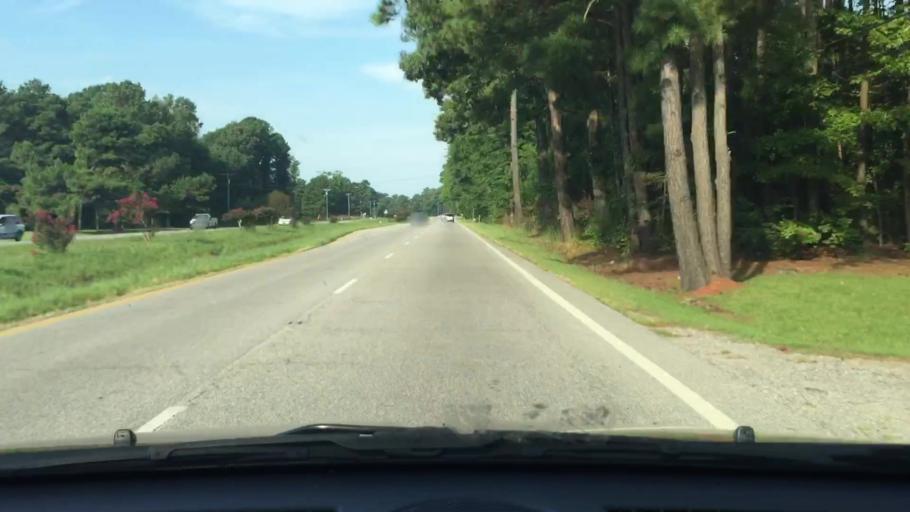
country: US
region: Virginia
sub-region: Isle of Wight County
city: Carrollton
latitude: 36.9414
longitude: -76.5664
